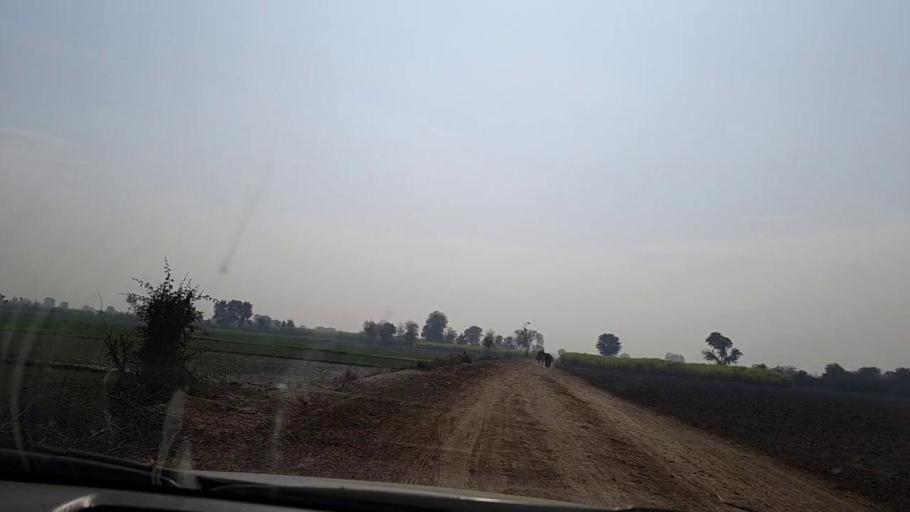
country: PK
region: Sindh
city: Daulatpur
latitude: 26.5416
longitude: 67.9876
